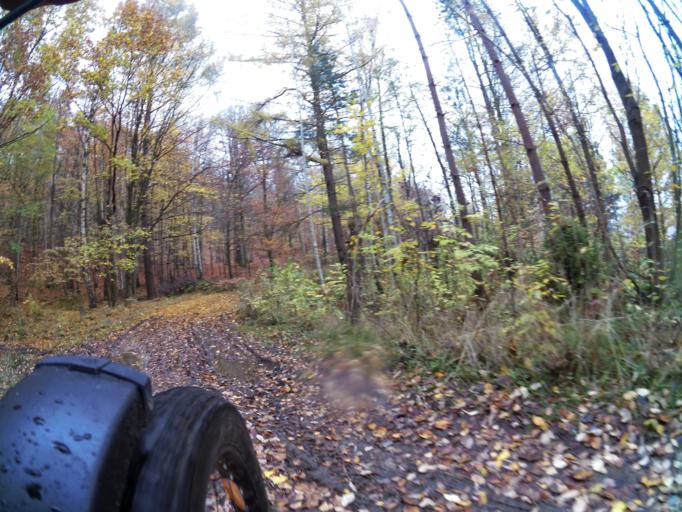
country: PL
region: Pomeranian Voivodeship
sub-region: Powiat wejherowski
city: Gniewino
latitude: 54.7542
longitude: 18.0838
